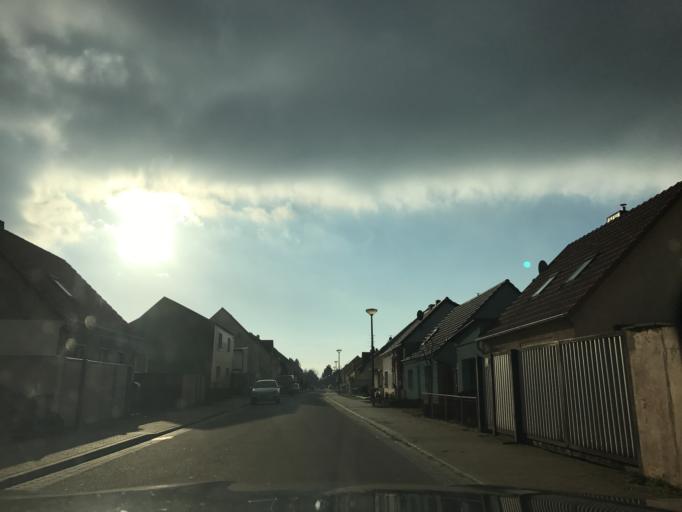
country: DE
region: Brandenburg
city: Brandenburg an der Havel
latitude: 52.3678
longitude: 12.5458
